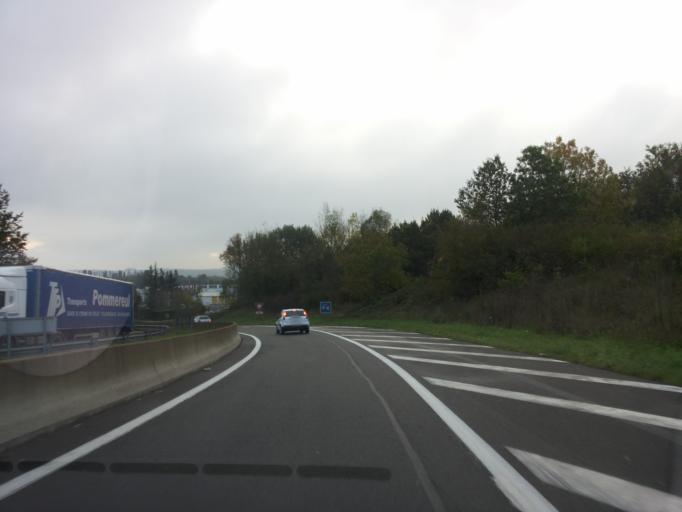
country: FR
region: Champagne-Ardenne
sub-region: Departement des Ardennes
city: Villers-Semeuse
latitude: 49.7354
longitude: 4.7478
